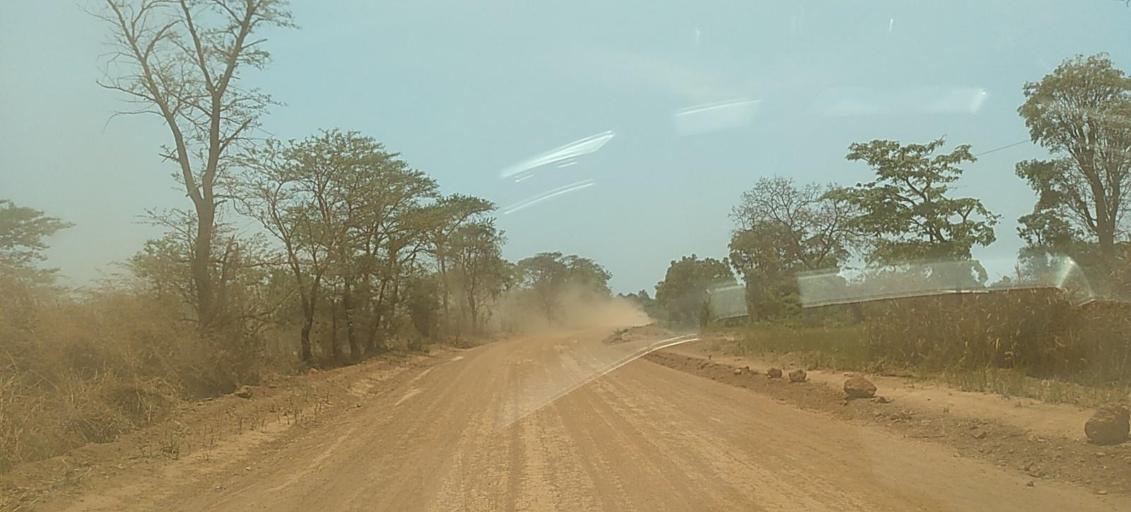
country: CD
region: Katanga
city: Kipushi
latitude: -11.8633
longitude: 27.1147
